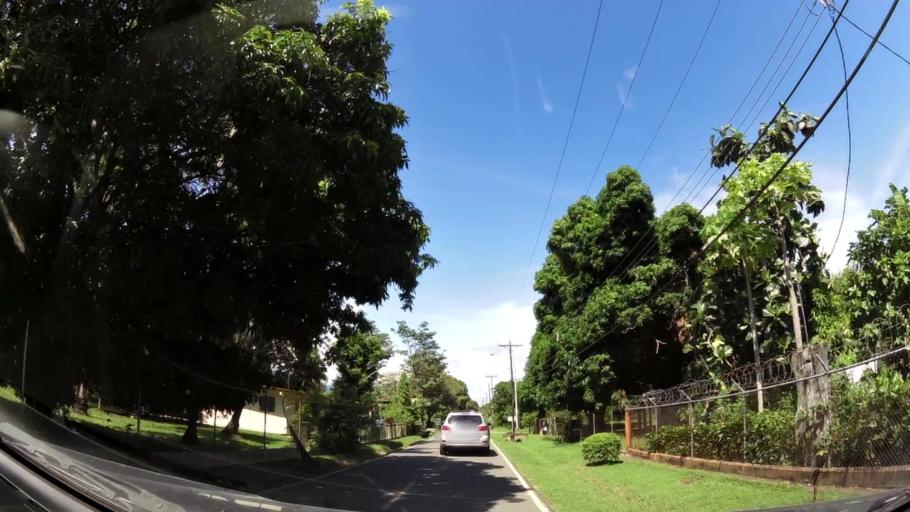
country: PA
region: Panama
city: Nueva Gorgona
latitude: 8.5518
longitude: -79.8751
